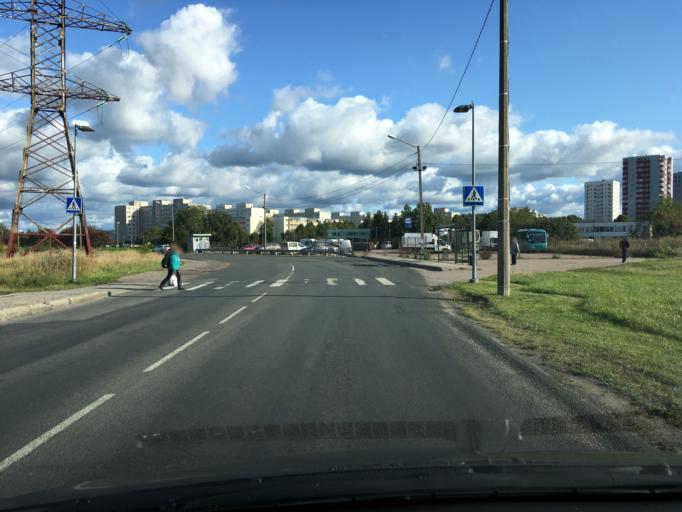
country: EE
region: Harju
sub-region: Tallinna linn
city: Kose
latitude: 59.4443
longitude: 24.8390
